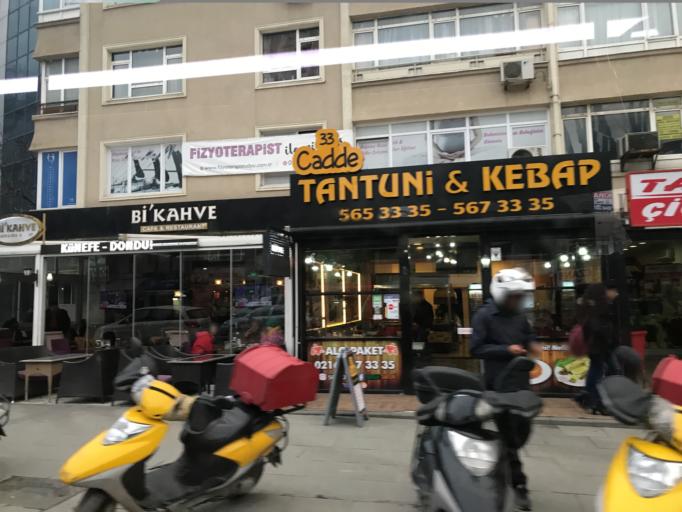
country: TR
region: Istanbul
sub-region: Atasehir
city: Atasehir
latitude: 40.9828
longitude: 29.0648
